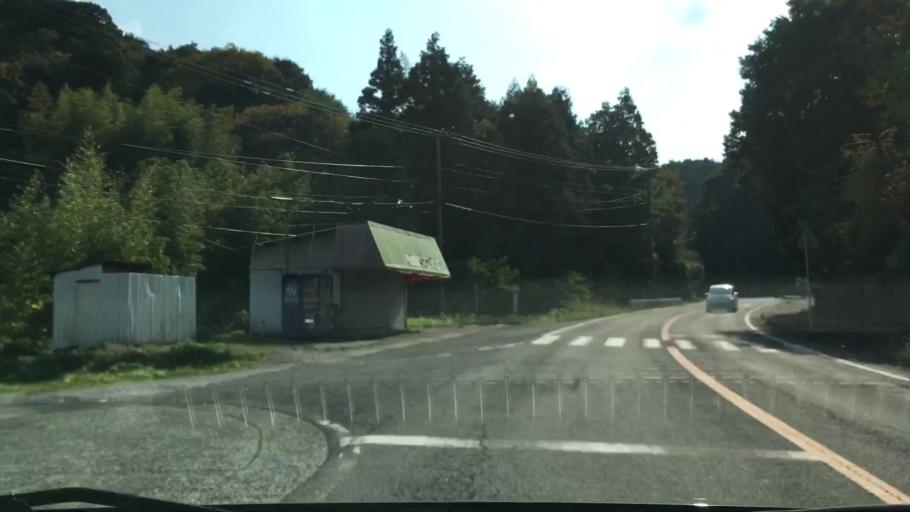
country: JP
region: Nagasaki
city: Togitsu
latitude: 32.9755
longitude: 129.7818
